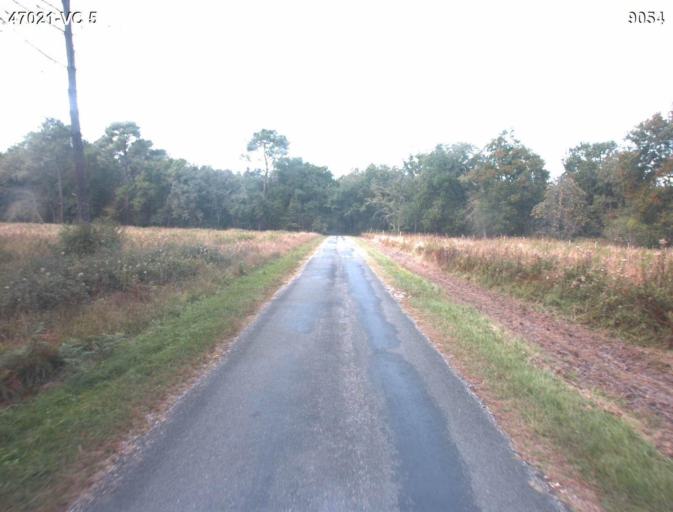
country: FR
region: Aquitaine
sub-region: Departement du Lot-et-Garonne
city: Barbaste
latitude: 44.1575
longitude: 0.1900
